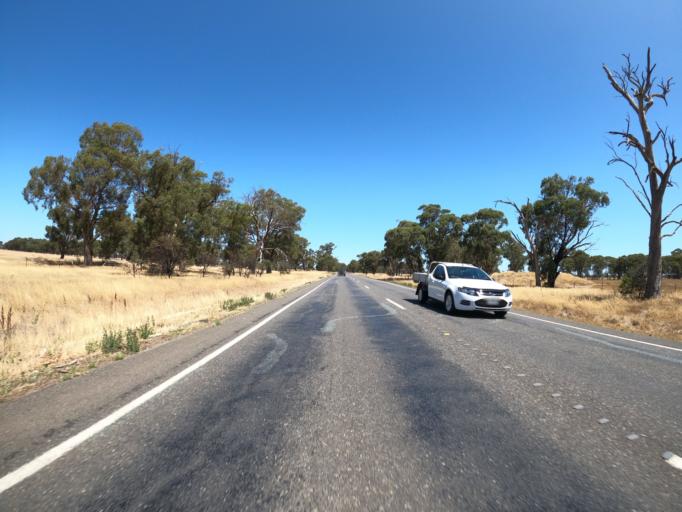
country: AU
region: New South Wales
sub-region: Corowa Shire
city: Corowa
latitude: -36.0233
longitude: 146.4150
